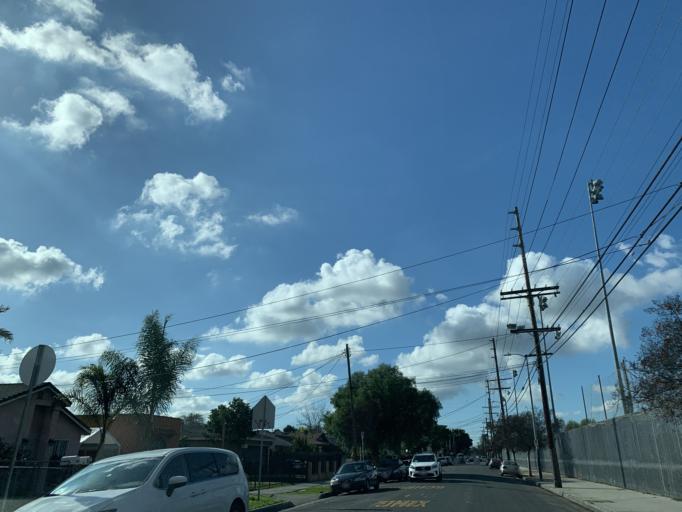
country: US
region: California
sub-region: Los Angeles County
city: Willowbrook
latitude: 33.9379
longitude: -118.2443
